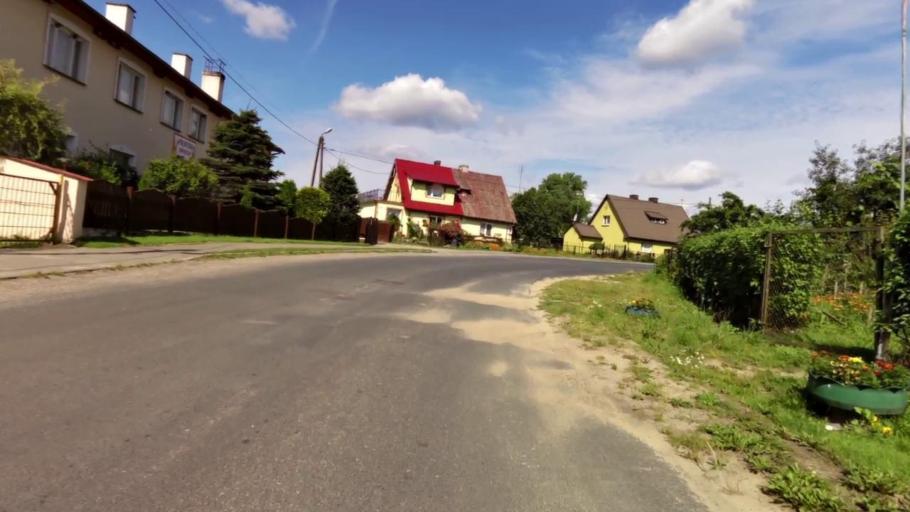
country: PL
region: West Pomeranian Voivodeship
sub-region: Powiat stargardzki
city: Dobrzany
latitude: 53.3813
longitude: 15.4360
